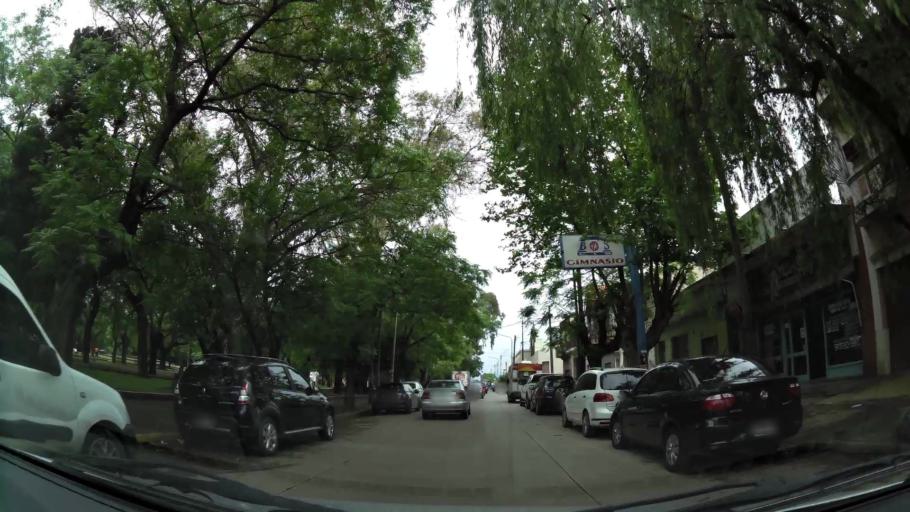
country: AR
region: Buenos Aires
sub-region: Partido de Lanus
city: Lanus
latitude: -34.7149
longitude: -58.3742
